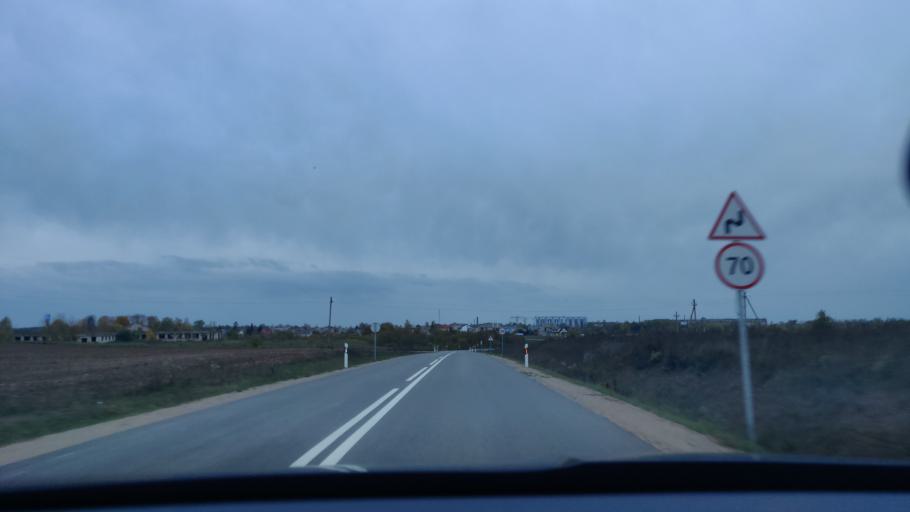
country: LT
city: Trakai
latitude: 54.6067
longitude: 24.9965
